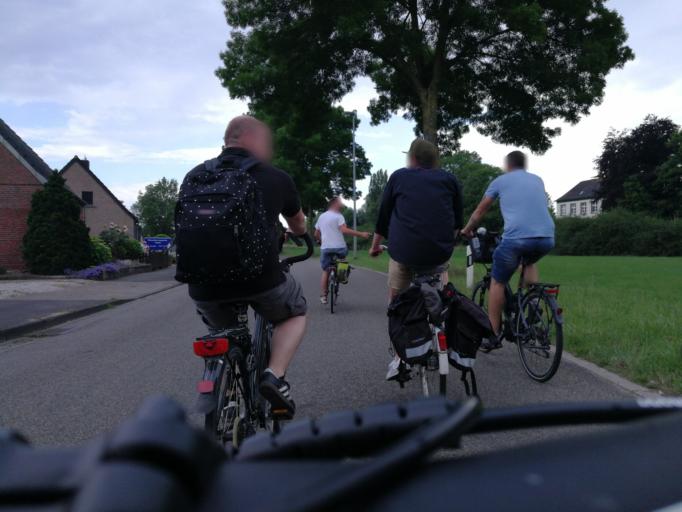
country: DE
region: North Rhine-Westphalia
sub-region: Regierungsbezirk Dusseldorf
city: Kleve
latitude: 51.8053
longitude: 6.1461
